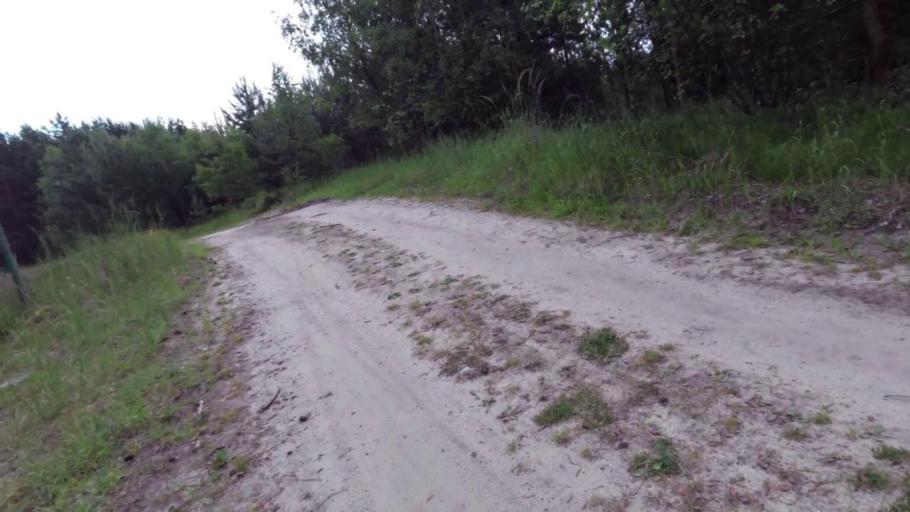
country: PL
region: West Pomeranian Voivodeship
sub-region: Swinoujscie
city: Swinoujscie
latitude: 53.9007
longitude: 14.3370
